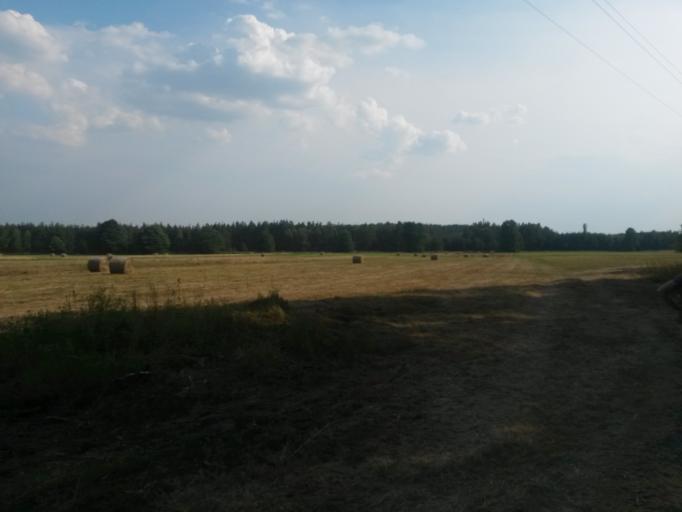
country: PL
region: Silesian Voivodeship
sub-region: Powiat czestochowski
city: Potok Zloty
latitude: 50.7320
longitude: 19.4525
